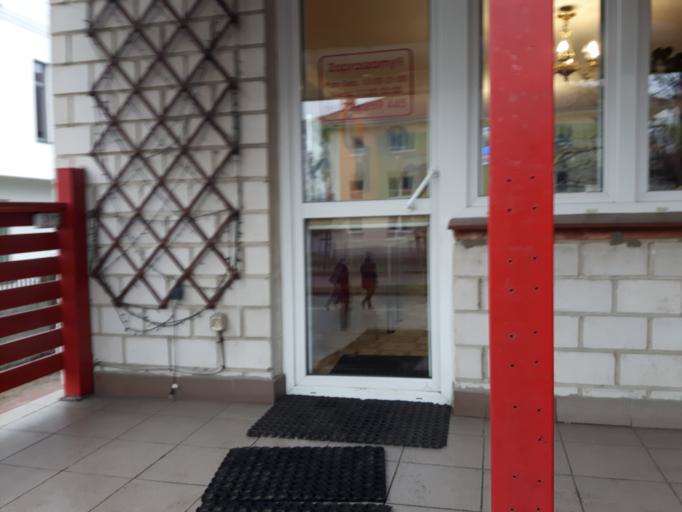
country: PL
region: Masovian Voivodeship
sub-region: Powiat wolominski
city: Zabki
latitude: 52.2790
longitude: 21.1239
